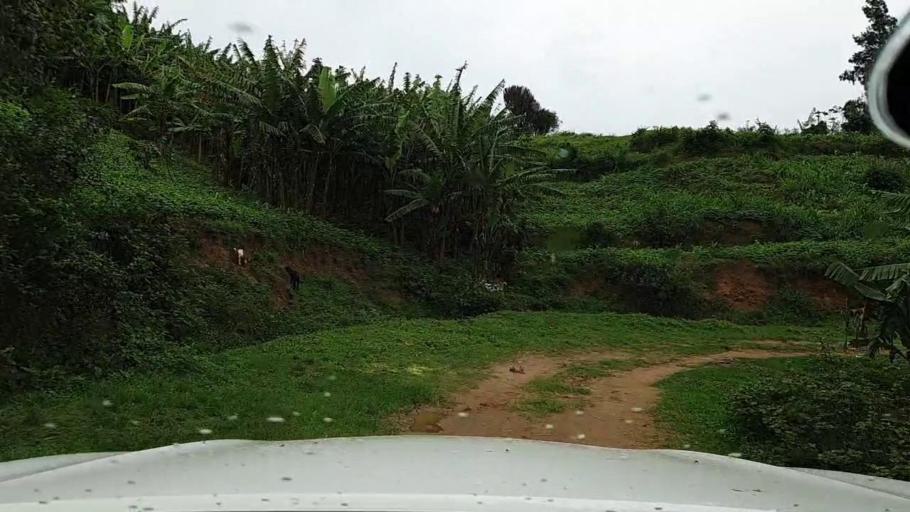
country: RW
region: Kigali
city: Kigali
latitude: -1.8984
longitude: 29.9531
